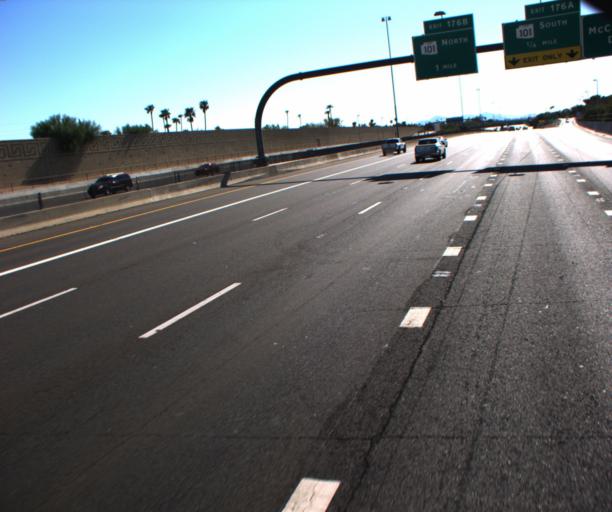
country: US
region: Arizona
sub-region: Maricopa County
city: Tempe
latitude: 33.3855
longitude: -111.9158
